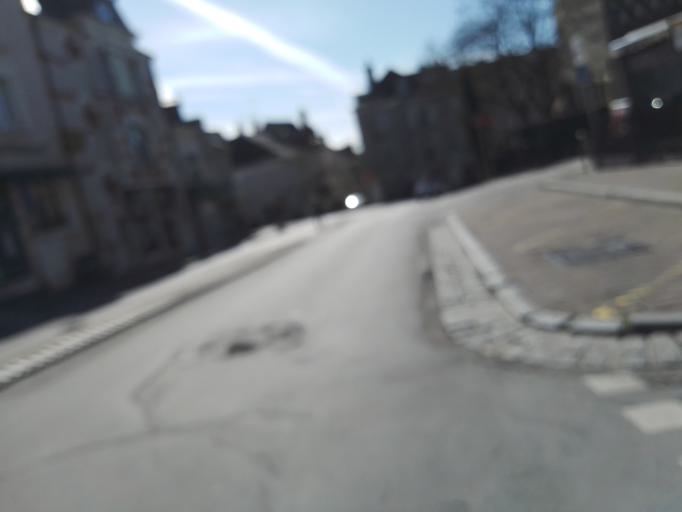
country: FR
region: Centre
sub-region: Departement du Loir-et-Cher
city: Blois
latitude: 47.5891
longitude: 1.3312
